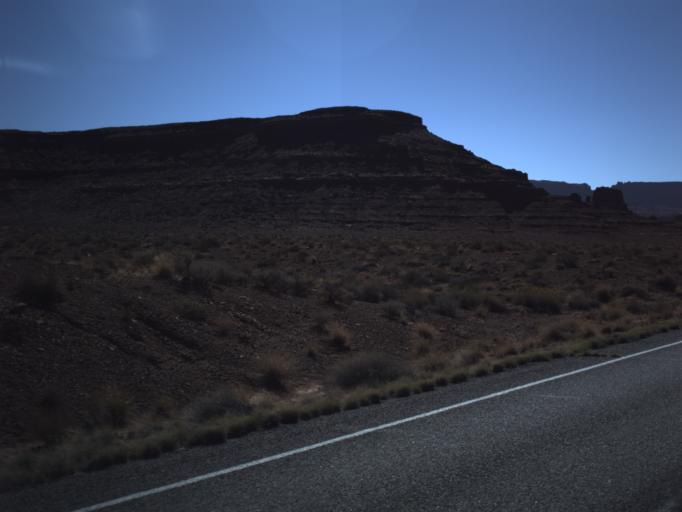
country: US
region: Utah
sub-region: San Juan County
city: Blanding
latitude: 37.8457
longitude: -110.3549
